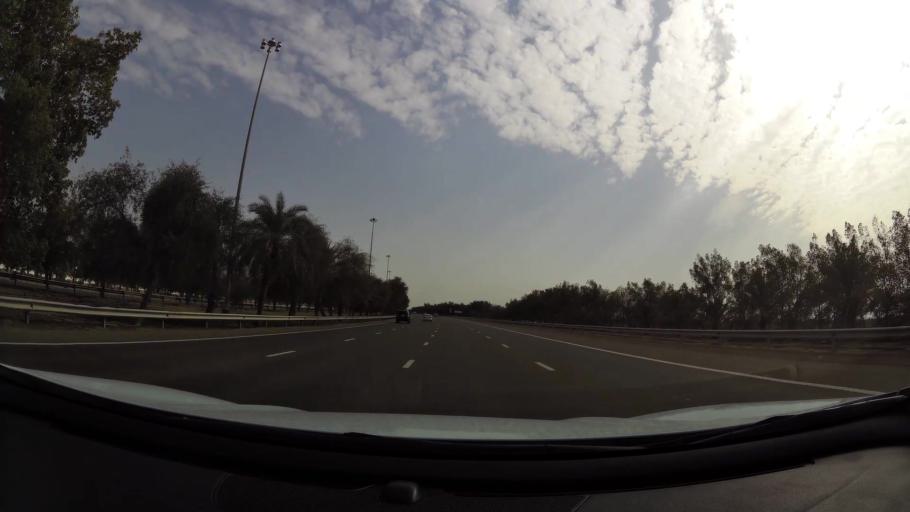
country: AE
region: Abu Dhabi
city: Abu Dhabi
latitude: 24.4825
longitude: 54.6750
